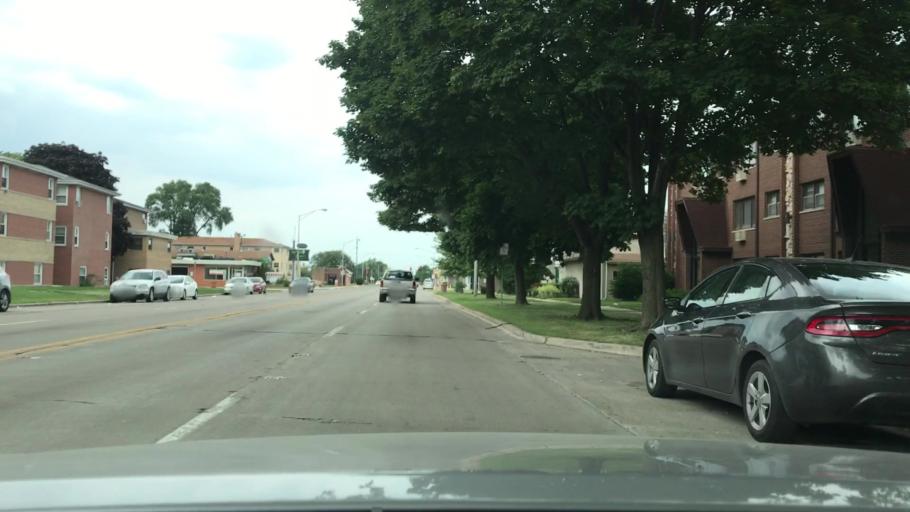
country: US
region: Illinois
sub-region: Cook County
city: Evergreen Park
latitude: 41.7254
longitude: -87.7019
